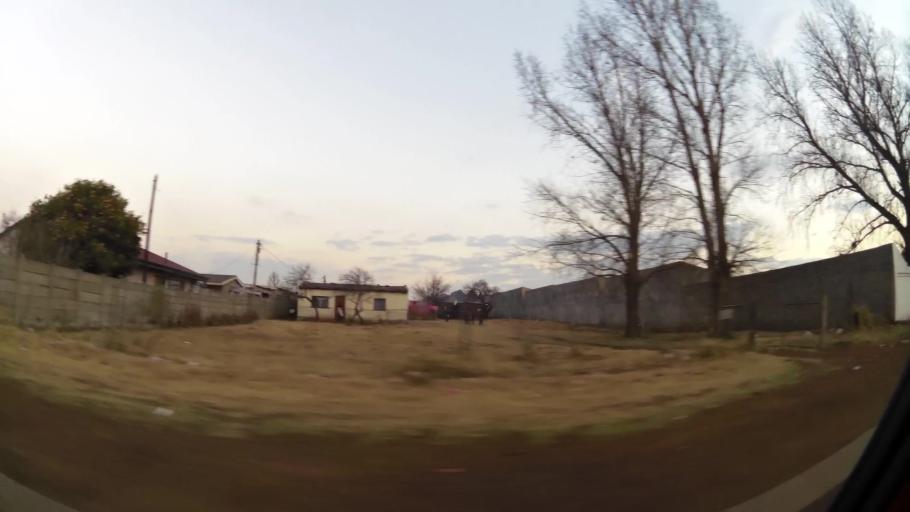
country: ZA
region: Gauteng
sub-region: City of Johannesburg Metropolitan Municipality
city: Orange Farm
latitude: -26.5470
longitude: 27.8369
